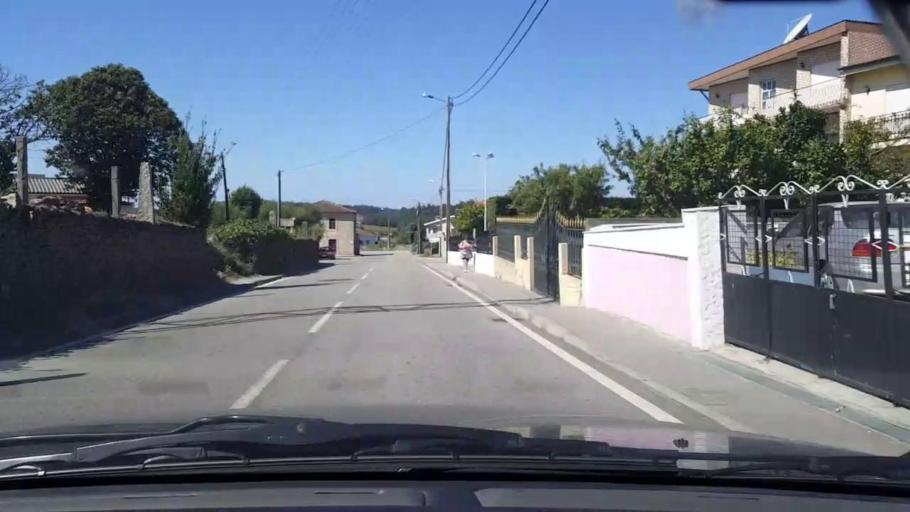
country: PT
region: Porto
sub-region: Vila do Conde
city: Arvore
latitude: 41.3418
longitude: -8.6637
